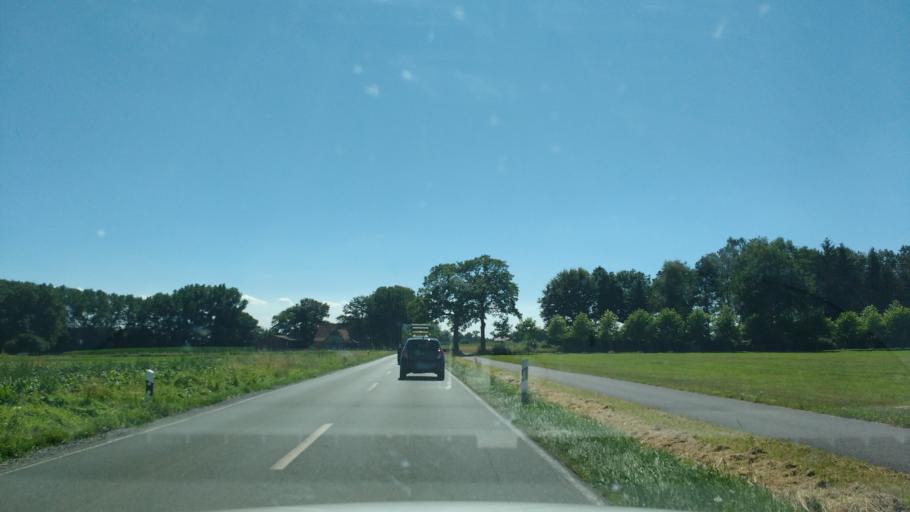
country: DE
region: North Rhine-Westphalia
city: Rietberg
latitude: 51.7150
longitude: 8.4361
